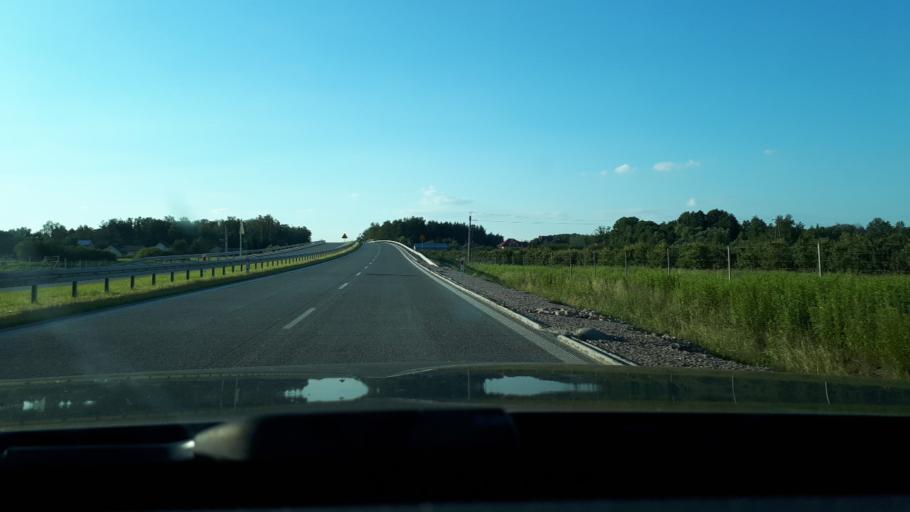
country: PL
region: Masovian Voivodeship
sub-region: Powiat piaseczynski
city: Baniocha
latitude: 51.9906
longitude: 21.1717
